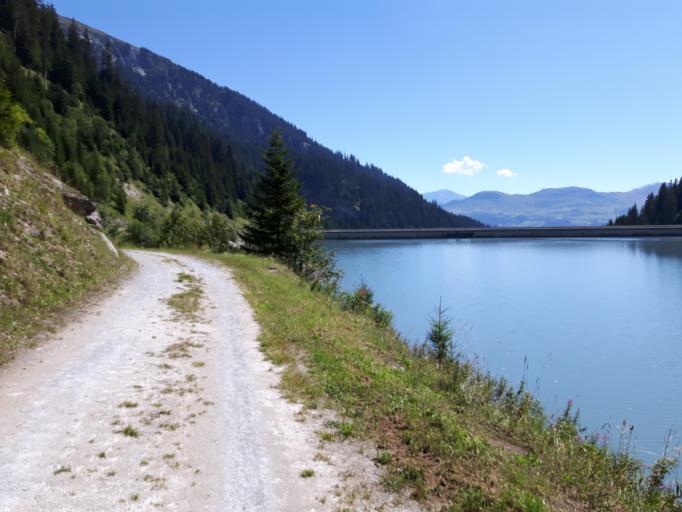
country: CH
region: Grisons
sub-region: Surselva District
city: Breil
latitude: 46.8277
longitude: 9.1083
